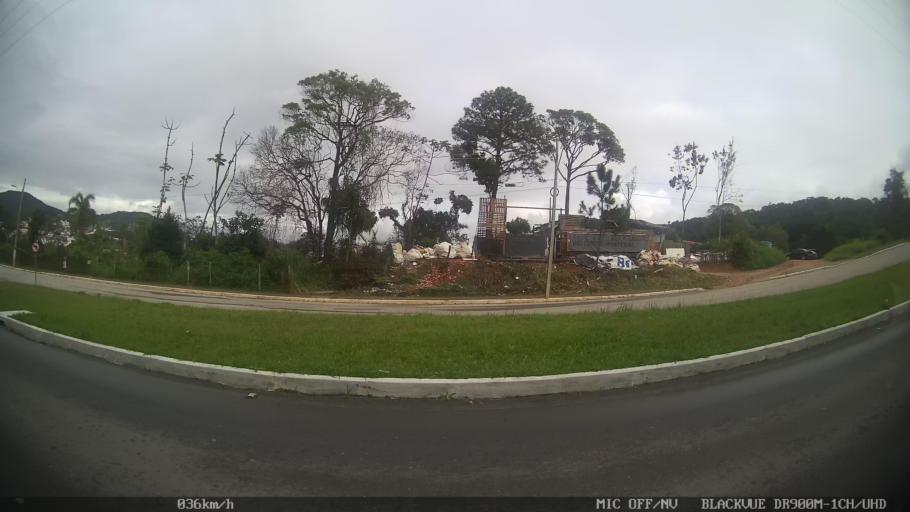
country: BR
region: Santa Catarina
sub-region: Sao Jose
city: Campinas
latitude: -27.5549
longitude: -48.6427
